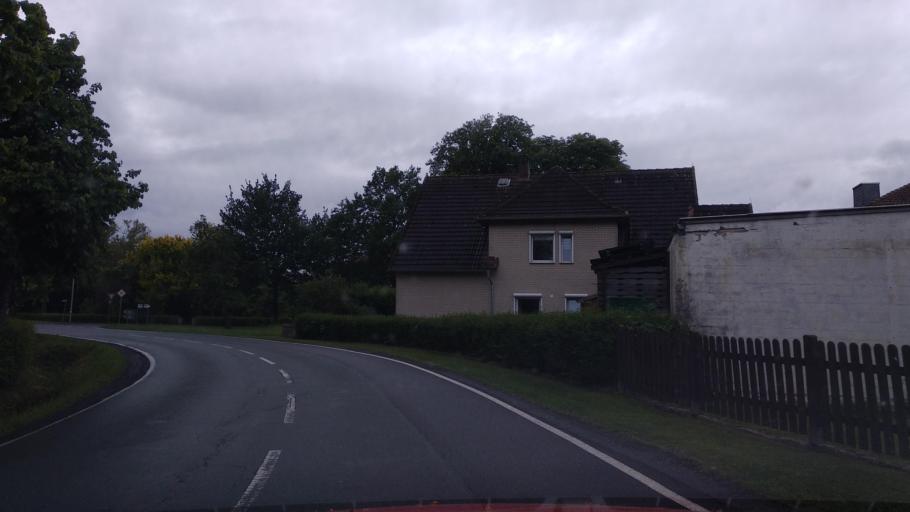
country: DE
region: Lower Saxony
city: Ludersfeld
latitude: 52.3654
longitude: 9.2516
